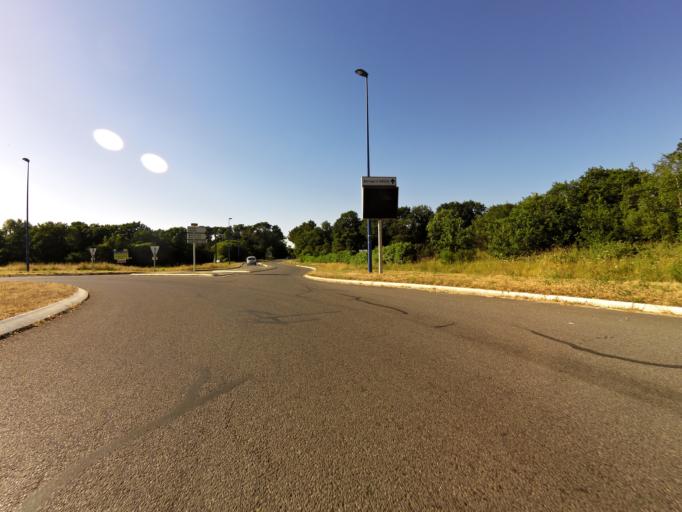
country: FR
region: Brittany
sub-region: Departement du Morbihan
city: Ferel
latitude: 47.4831
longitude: -2.3853
